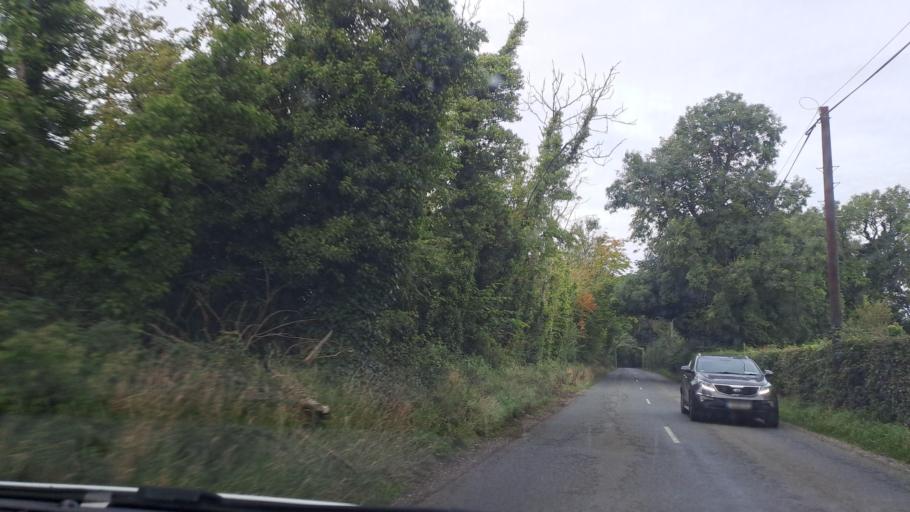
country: IE
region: Ulster
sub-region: County Monaghan
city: Carrickmacross
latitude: 53.8565
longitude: -6.6680
